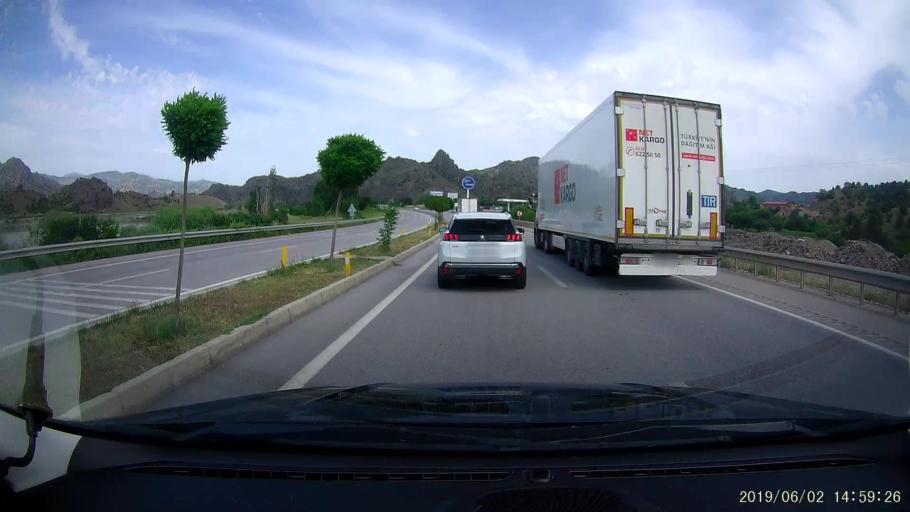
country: TR
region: Corum
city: Osmancik
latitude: 40.9714
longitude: 34.6956
